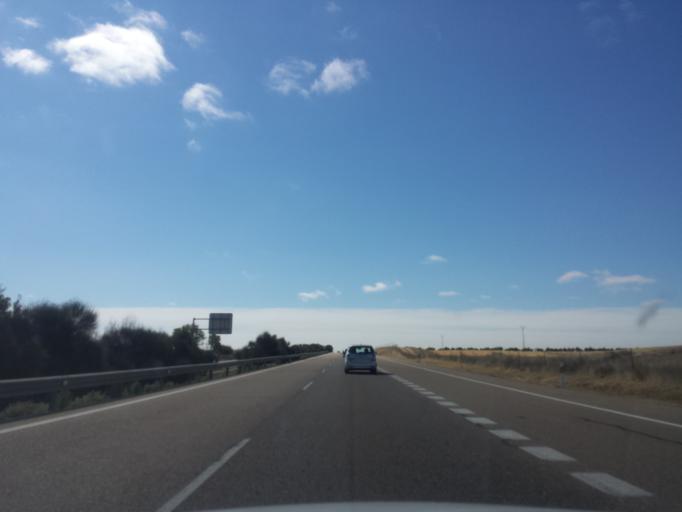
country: ES
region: Castille and Leon
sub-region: Provincia de Valladolid
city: Uruena
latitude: 41.6767
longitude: -5.2054
